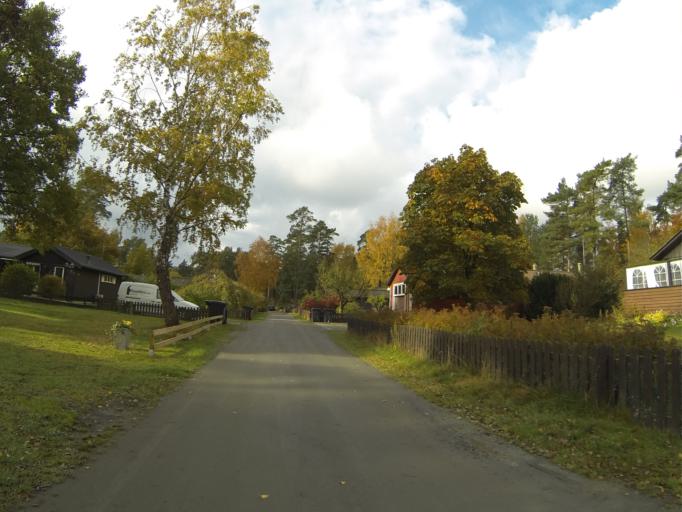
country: SE
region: Skane
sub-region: Sjobo Kommun
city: Sjoebo
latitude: 55.6319
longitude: 13.6451
